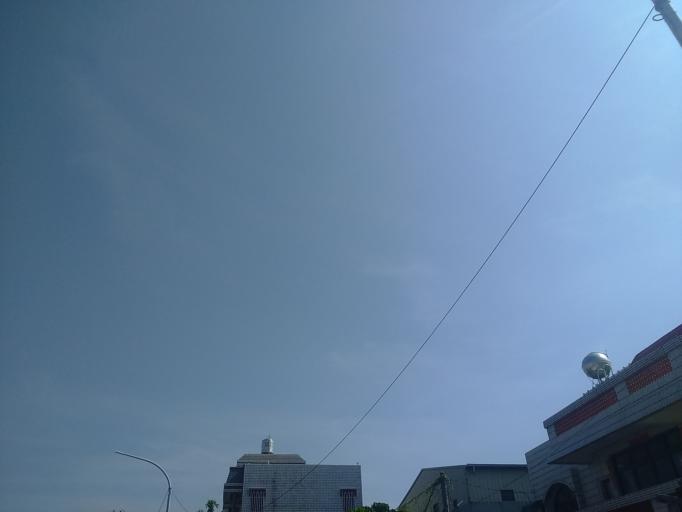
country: TW
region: Taiwan
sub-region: Chiayi
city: Jiayi Shi
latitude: 23.4728
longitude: 120.4173
